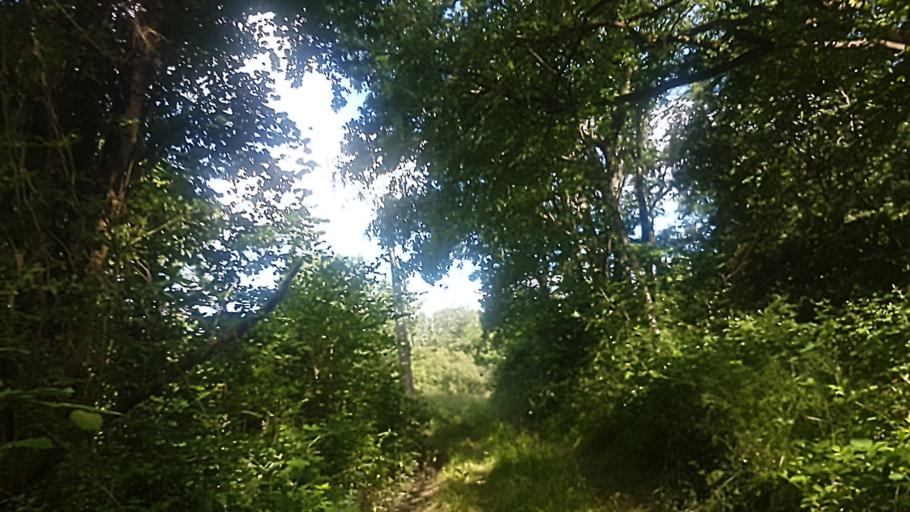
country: BE
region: Wallonia
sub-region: Province de Namur
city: Couvin
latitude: 50.0580
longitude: 4.5531
